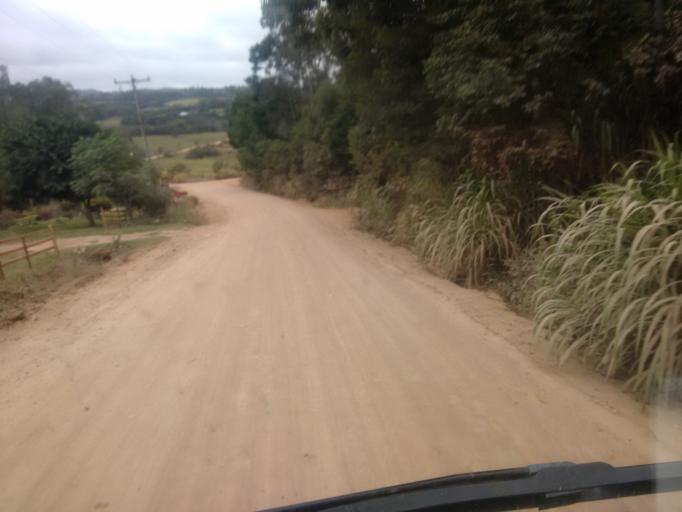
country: BR
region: Rio Grande do Sul
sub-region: Camaqua
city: Camaqua
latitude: -30.7587
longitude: -51.8718
